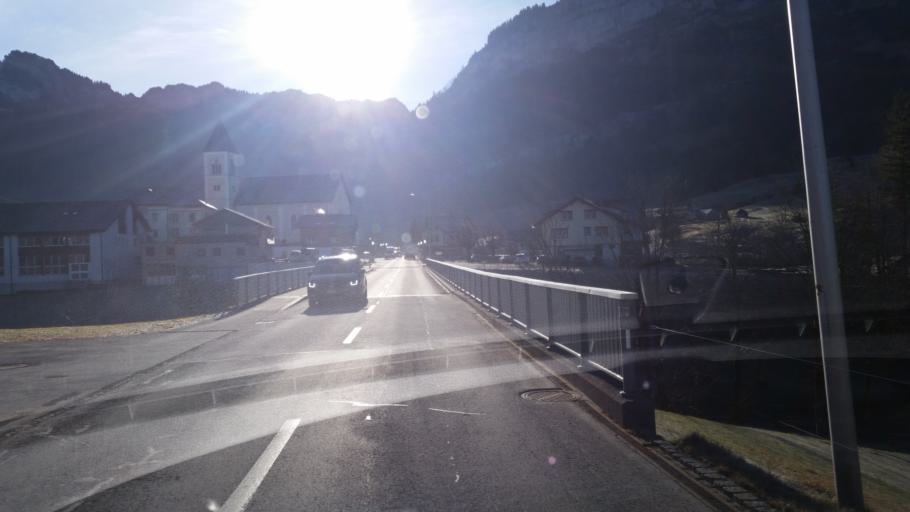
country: CH
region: Appenzell Innerrhoden
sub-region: Appenzell Inner Rhodes
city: Appenzell
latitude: 47.2990
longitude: 9.4549
